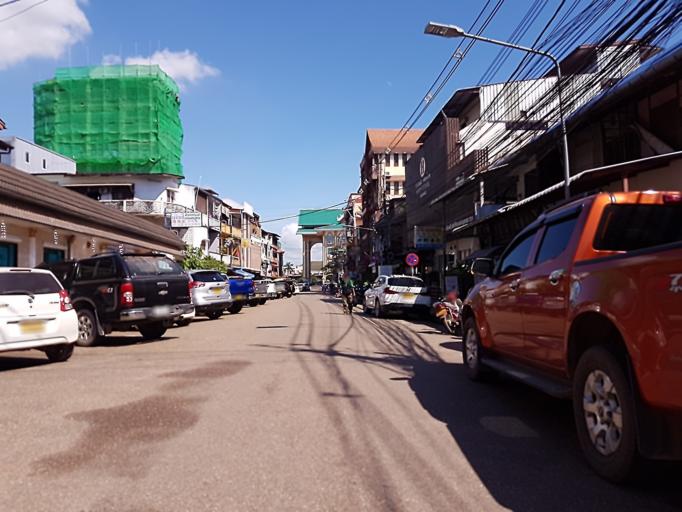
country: LA
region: Vientiane
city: Vientiane
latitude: 17.9671
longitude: 102.6051
